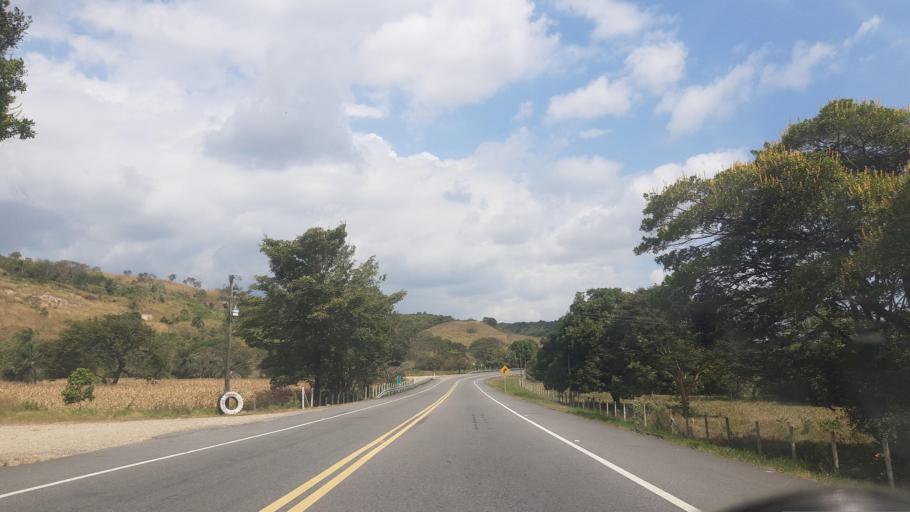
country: CO
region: Casanare
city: Tauramena
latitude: 4.8722
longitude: -72.7048
